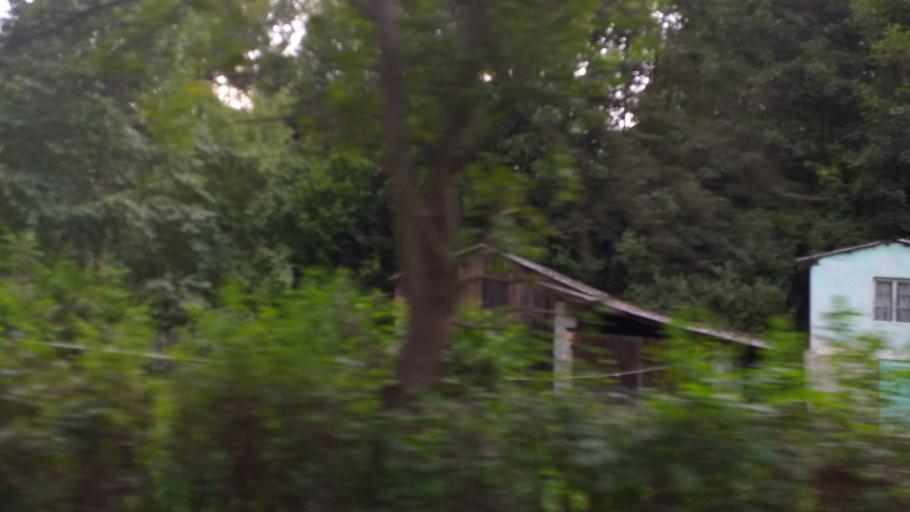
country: PL
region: Lower Silesian Voivodeship
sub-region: Powiat lubanski
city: Lesna
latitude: 51.0485
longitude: 15.2649
